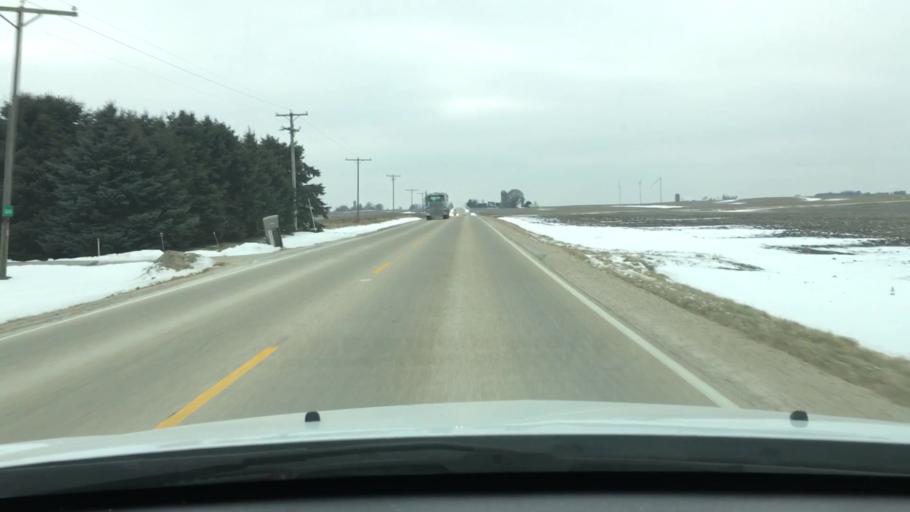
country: US
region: Illinois
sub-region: DeKalb County
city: Malta
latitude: 41.8487
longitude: -88.9006
